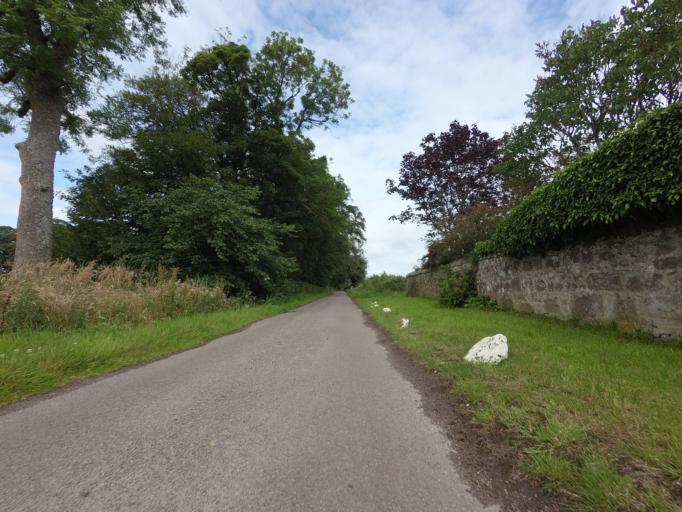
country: GB
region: Scotland
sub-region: Moray
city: Hopeman
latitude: 57.6727
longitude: -3.4018
